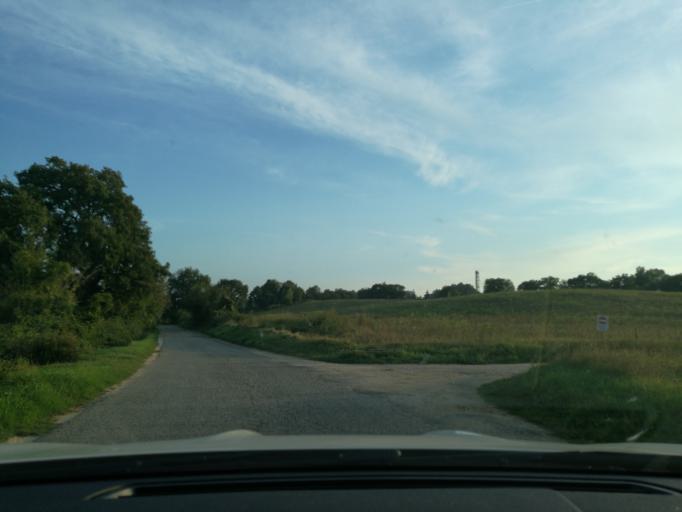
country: IT
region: Umbria
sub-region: Provincia di Terni
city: Acquasparta
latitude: 42.6804
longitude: 12.5480
